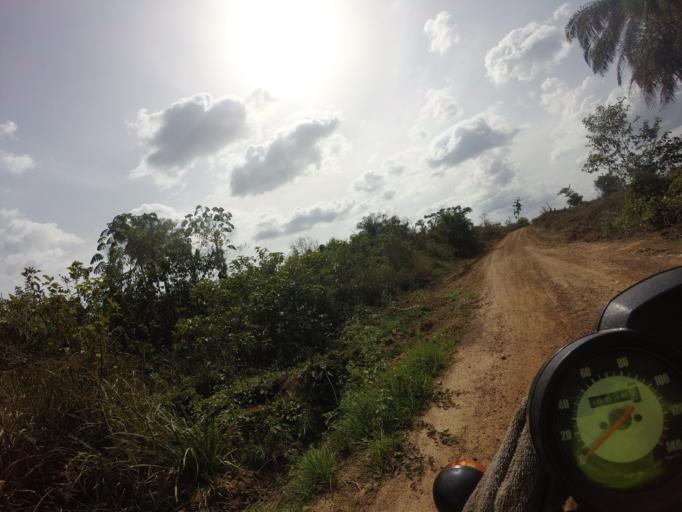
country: SL
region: Southern Province
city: Zimmi
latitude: 7.2232
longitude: -11.1874
